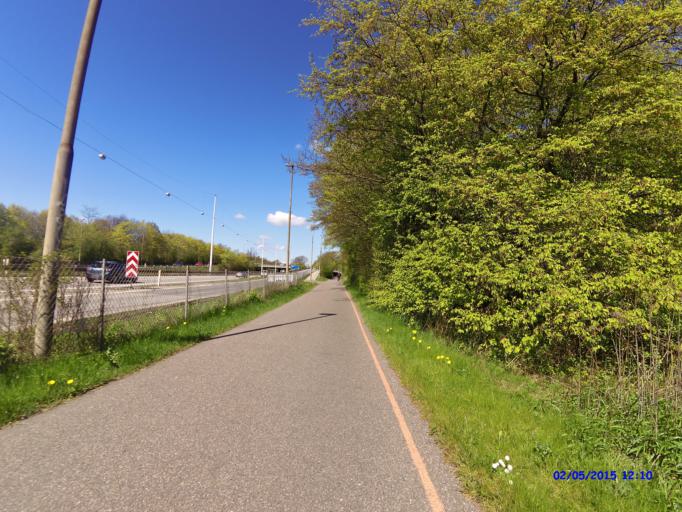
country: DK
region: Capital Region
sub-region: Gladsaxe Municipality
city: Buddinge
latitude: 55.7283
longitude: 12.4800
